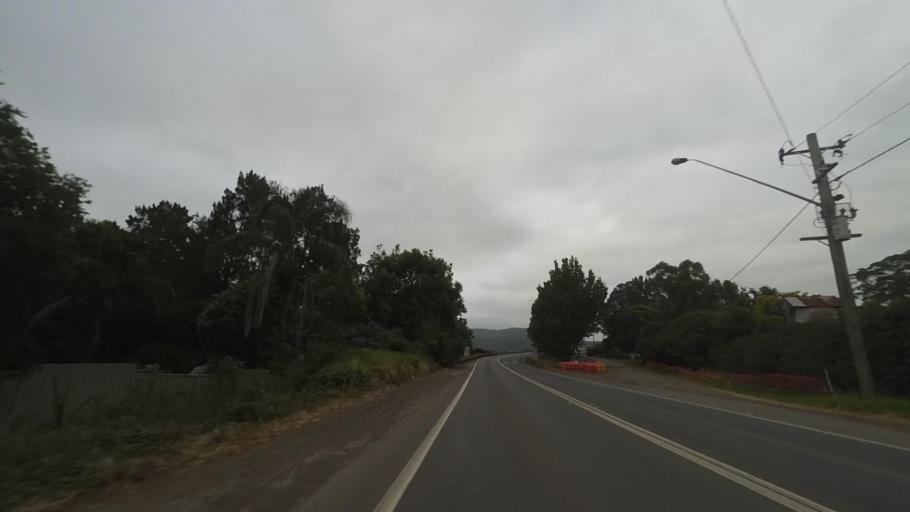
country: AU
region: New South Wales
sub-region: Shoalhaven Shire
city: Berry
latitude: -34.7733
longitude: 150.7053
